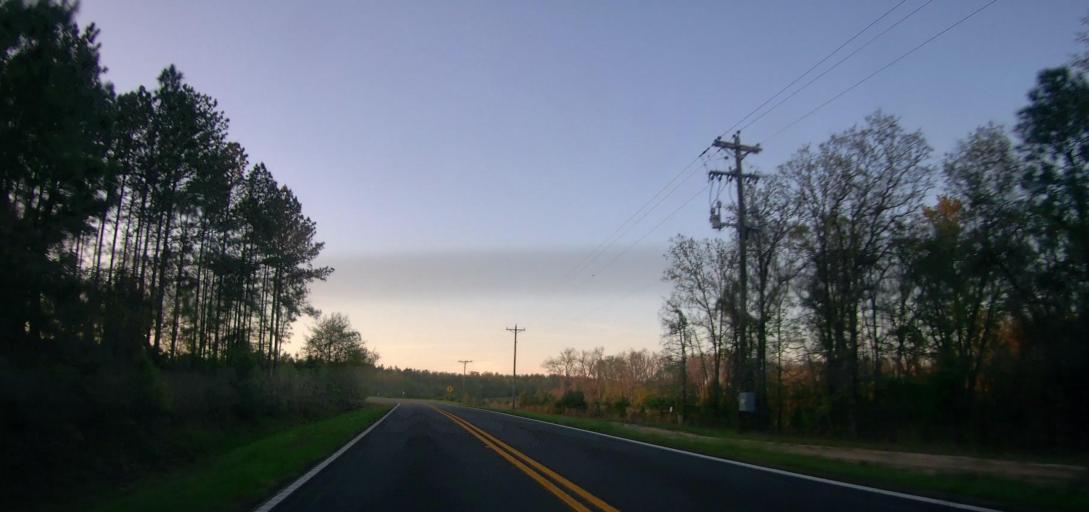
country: US
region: Georgia
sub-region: Marion County
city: Buena Vista
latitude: 32.4366
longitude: -84.5997
